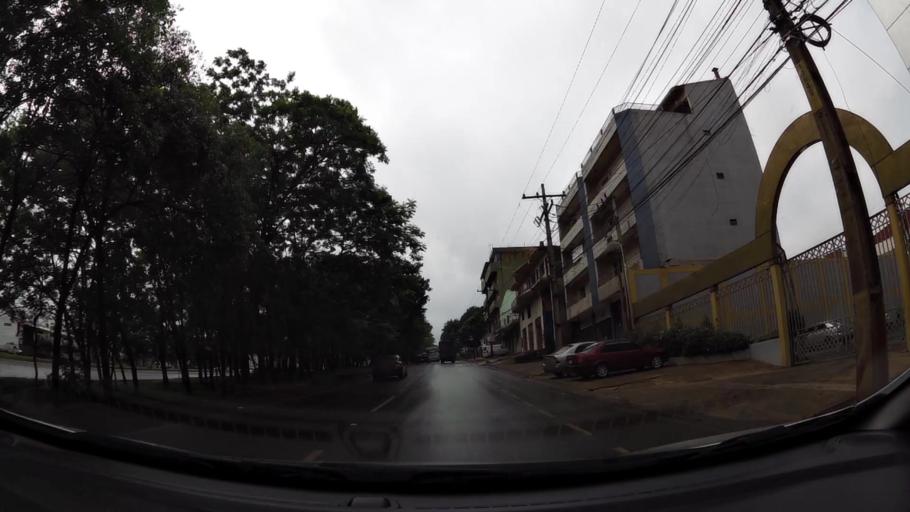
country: PY
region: Alto Parana
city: Ciudad del Este
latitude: -25.5042
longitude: -54.6491
